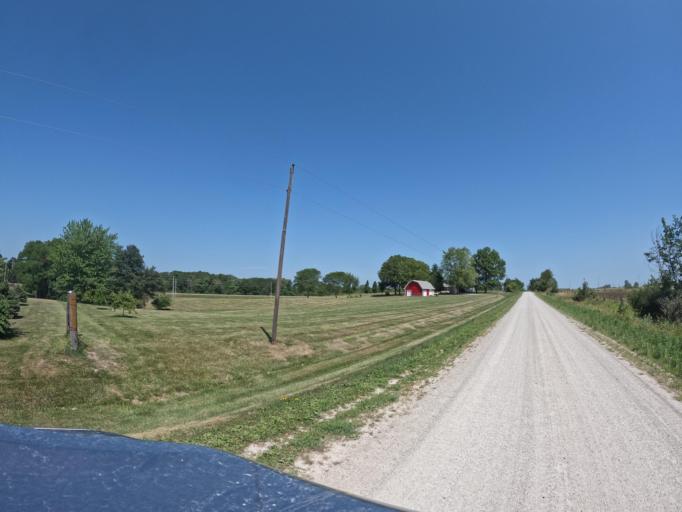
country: US
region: Iowa
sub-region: Henry County
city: Mount Pleasant
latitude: 40.9337
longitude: -91.5381
